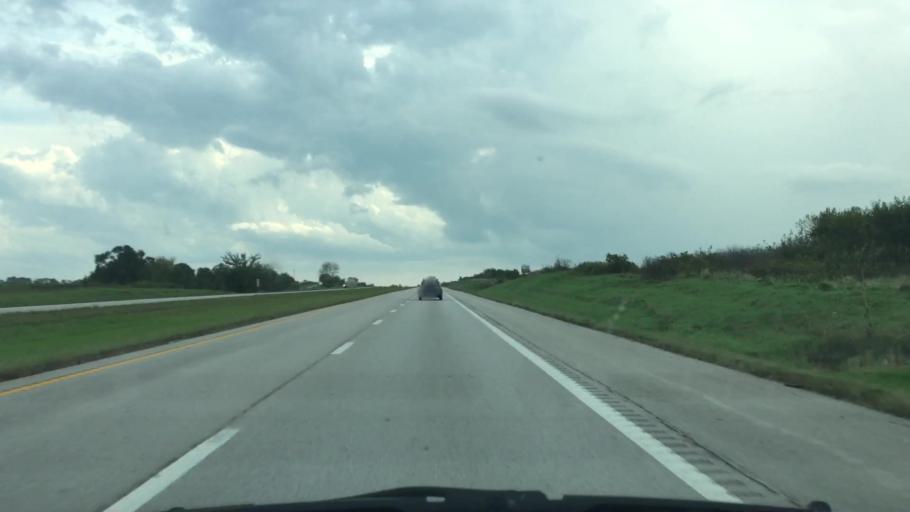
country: US
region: Missouri
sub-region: Clinton County
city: Cameron
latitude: 39.8017
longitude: -94.2002
